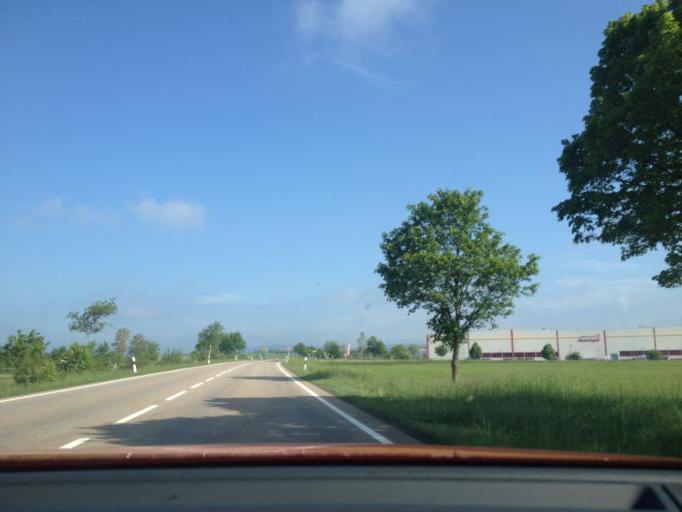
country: DE
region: Bavaria
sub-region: Upper Palatinate
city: Kemnath
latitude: 49.8588
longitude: 11.8796
